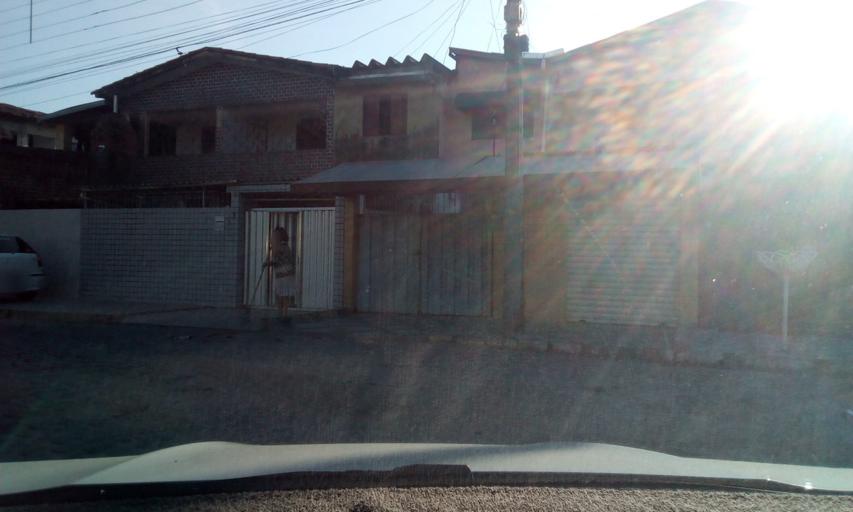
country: BR
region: Paraiba
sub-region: Joao Pessoa
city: Joao Pessoa
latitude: -7.1710
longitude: -34.8864
